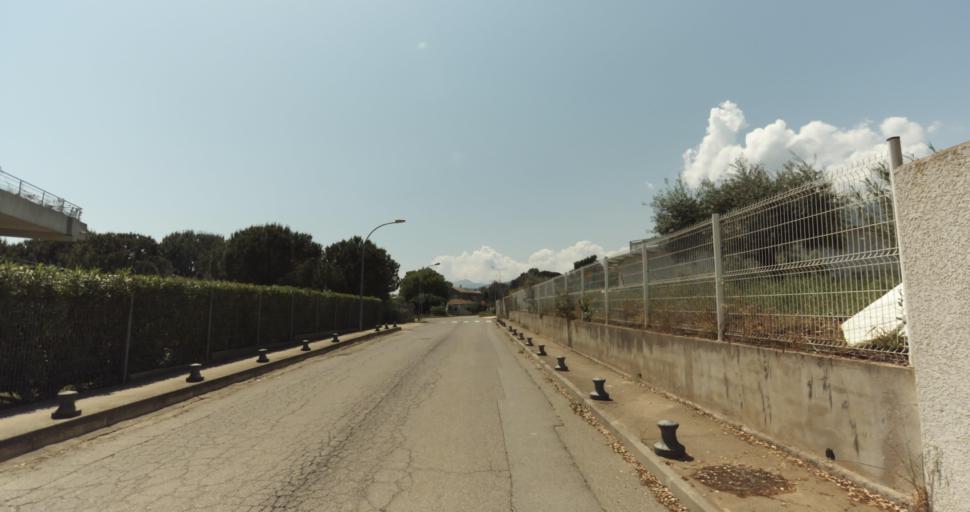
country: FR
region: Corsica
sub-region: Departement de la Haute-Corse
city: Biguglia
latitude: 42.5932
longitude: 9.4347
